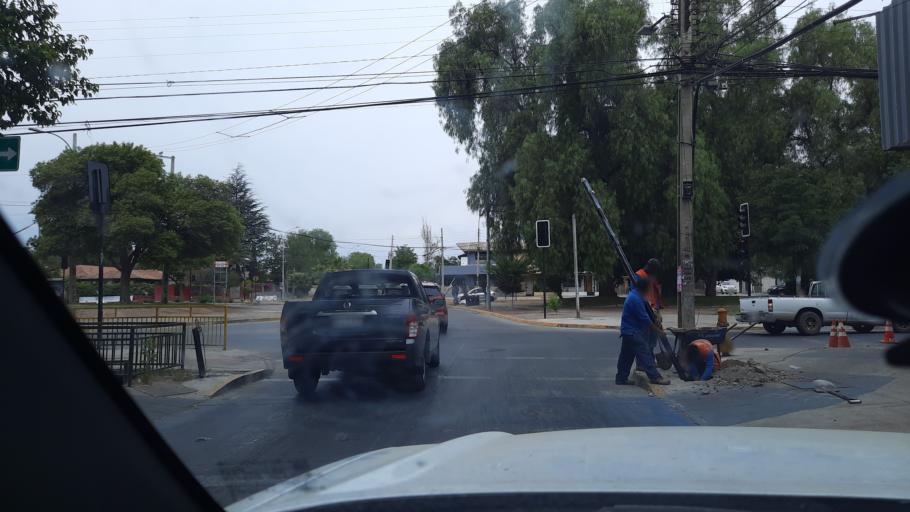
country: CL
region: Valparaiso
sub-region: Provincia de San Felipe
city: San Felipe
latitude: -32.7480
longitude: -70.7192
